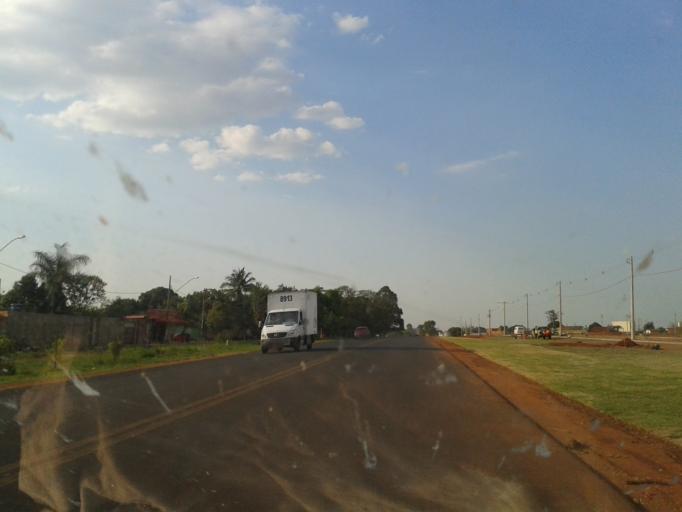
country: BR
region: Minas Gerais
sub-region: Uberlandia
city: Uberlandia
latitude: -18.9597
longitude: -48.3069
